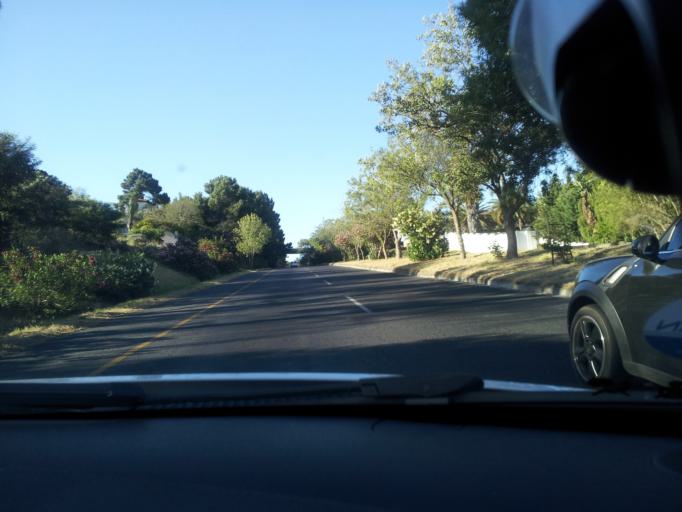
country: ZA
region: Western Cape
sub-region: Cape Winelands District Municipality
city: Stellenbosch
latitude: -34.0552
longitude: 18.8293
